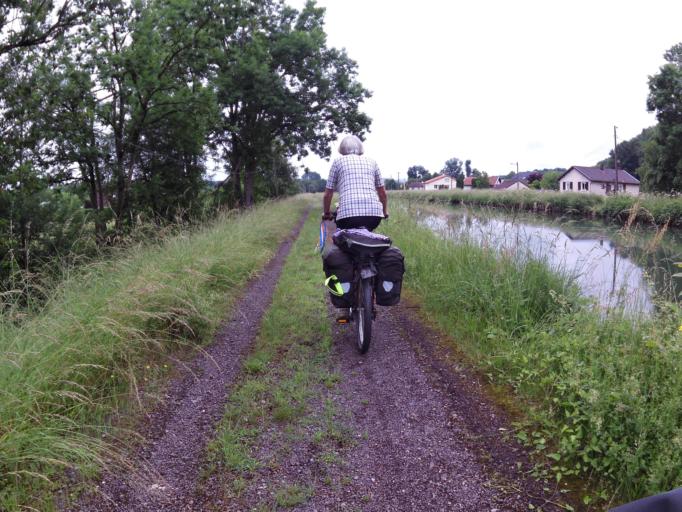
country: FR
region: Lorraine
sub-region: Departement de la Meuse
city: Fains-Veel
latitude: 48.7958
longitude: 5.1149
